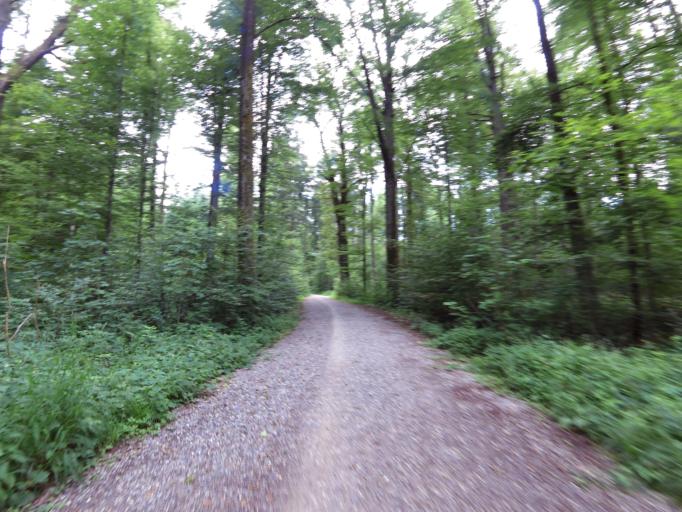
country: CH
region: Zurich
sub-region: Bezirk Zuerich
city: Zuerich (Kreis 10) / Ruetihof
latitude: 47.4163
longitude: 8.4904
